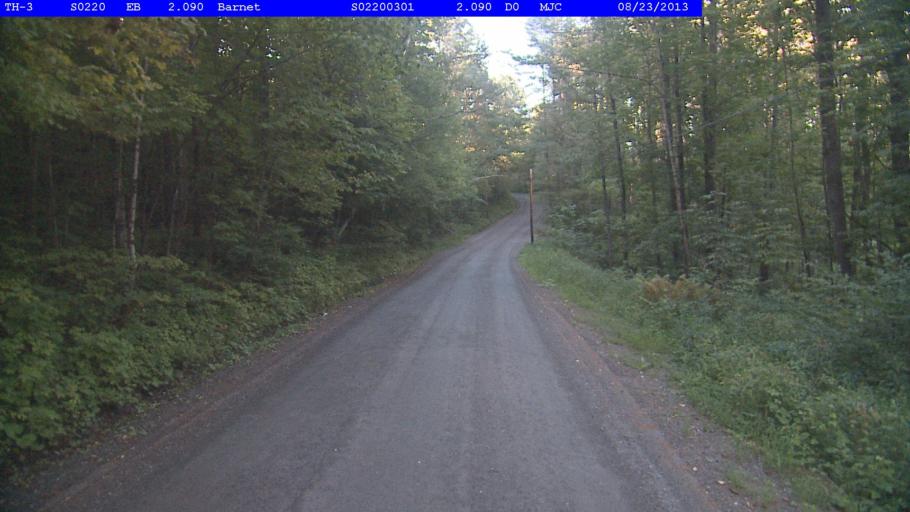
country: US
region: Vermont
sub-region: Caledonia County
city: Saint Johnsbury
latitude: 44.3288
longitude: -72.0175
